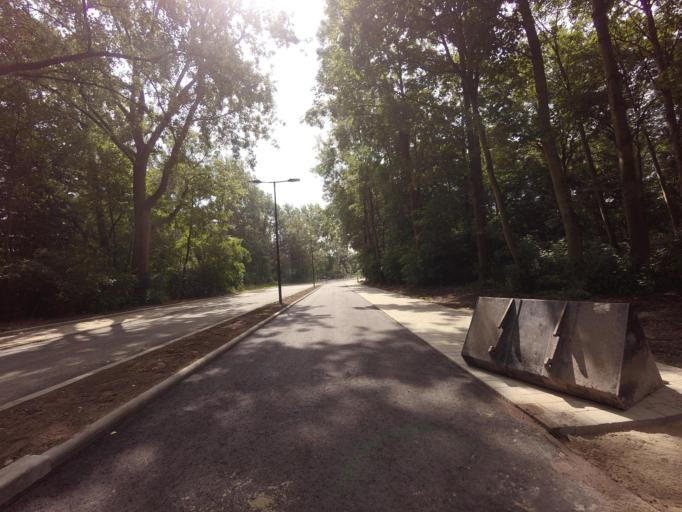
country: NL
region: South Holland
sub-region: Gemeente Schiedam
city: Schiedam
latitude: 51.9289
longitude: 4.3938
